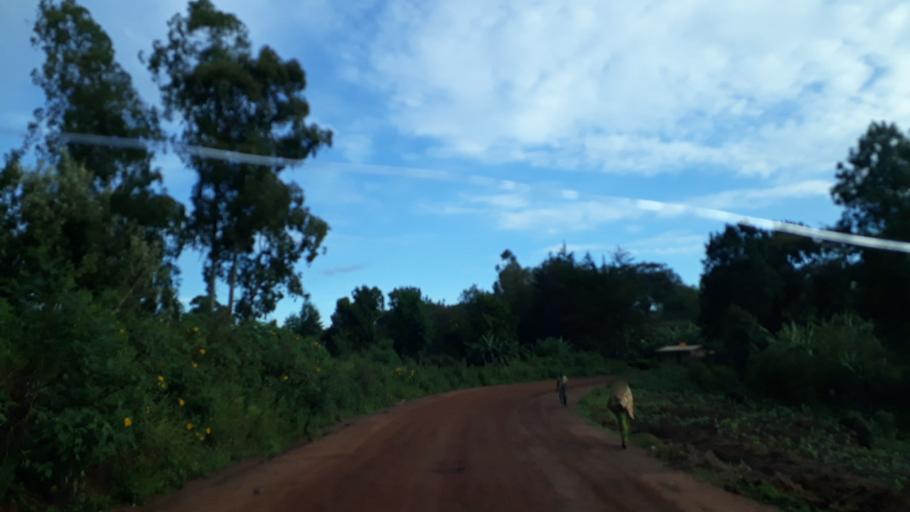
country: UG
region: Northern Region
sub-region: Zombo District
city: Paidha
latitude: 2.2421
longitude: 30.8609
